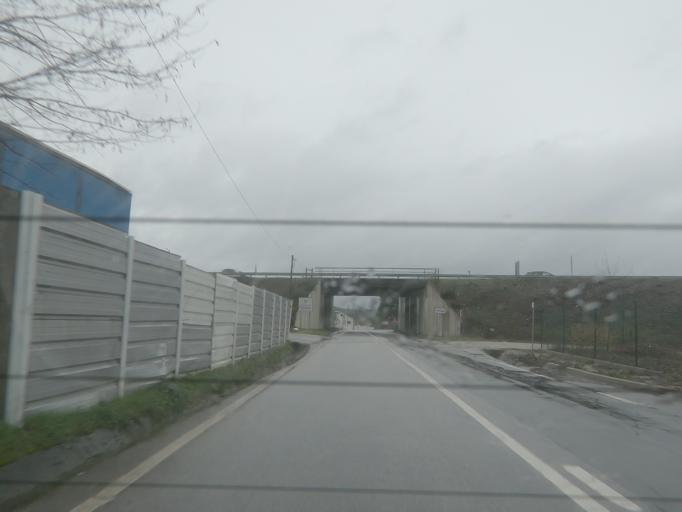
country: PT
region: Vila Real
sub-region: Vila Real
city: Vila Real
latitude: 41.2674
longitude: -7.6989
